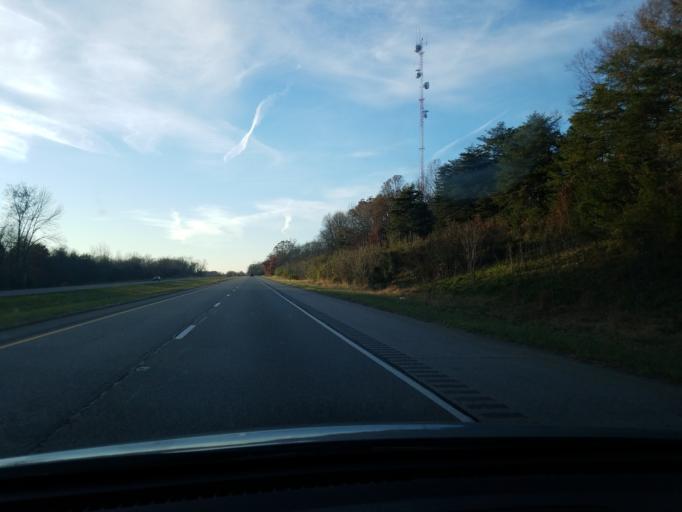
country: US
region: Indiana
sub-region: Warrick County
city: Boonville
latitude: 38.2015
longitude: -87.1999
